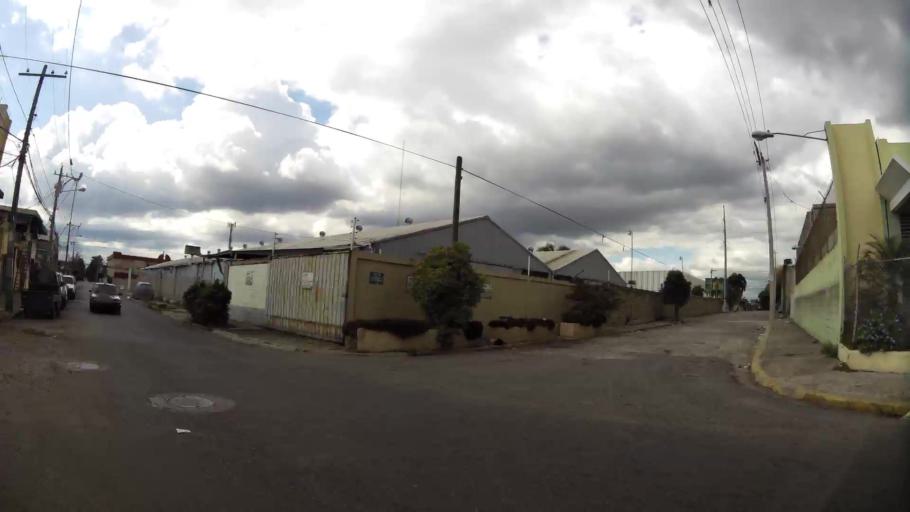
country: DO
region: Nacional
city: La Agustina
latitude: 18.4928
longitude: -69.9204
